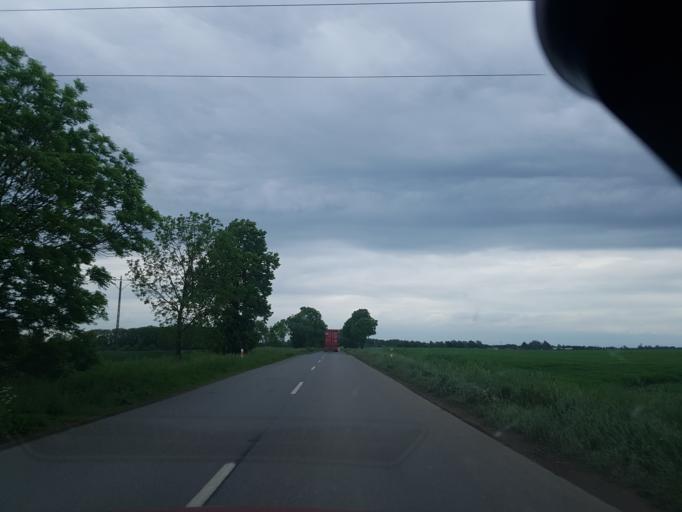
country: PL
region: Lower Silesian Voivodeship
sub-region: Powiat wroclawski
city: Zorawina
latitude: 50.9224
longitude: 17.0186
